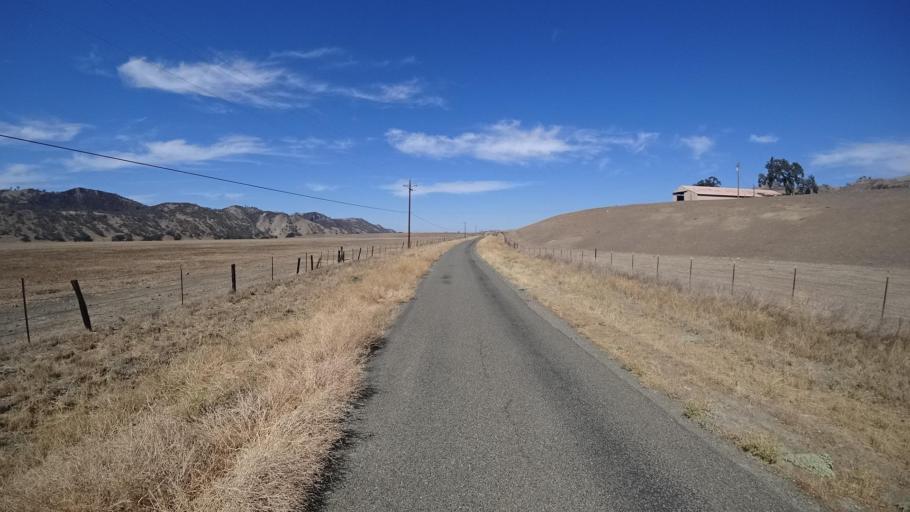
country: US
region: California
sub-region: Monterey County
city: King City
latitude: 36.1557
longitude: -120.7677
